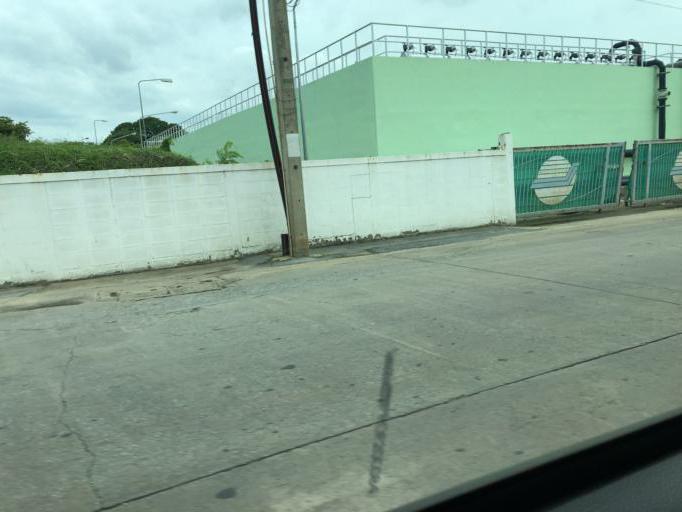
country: TH
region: Bangkok
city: Don Mueang
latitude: 13.9372
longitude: 100.6083
